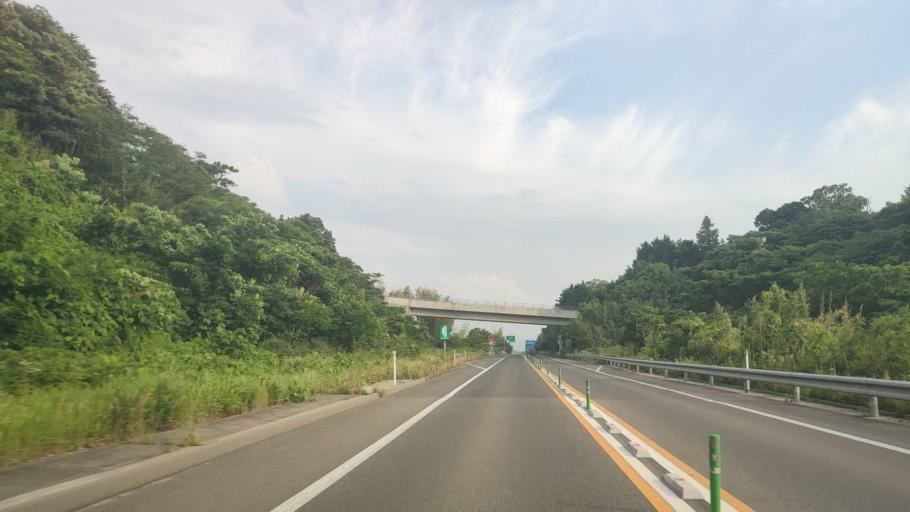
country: JP
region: Tottori
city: Kurayoshi
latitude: 35.4753
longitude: 133.8063
